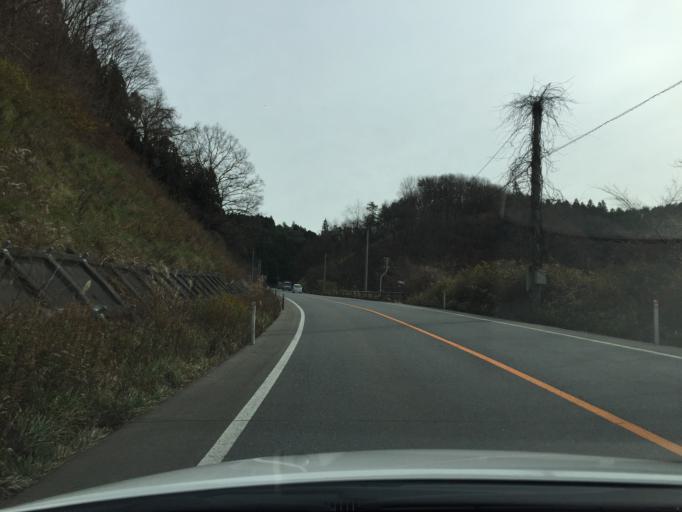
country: JP
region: Fukushima
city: Ishikawa
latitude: 37.2131
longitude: 140.6040
